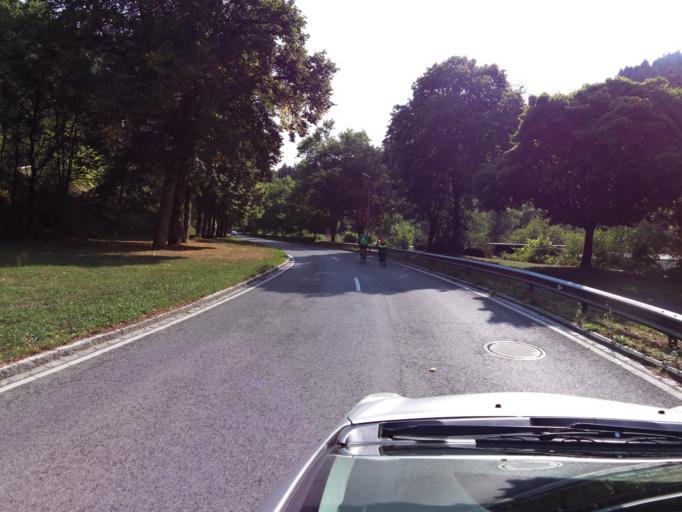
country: LU
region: Diekirch
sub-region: Canton de Wiltz
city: Esch-sur-Sure
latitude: 49.9067
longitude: 5.9396
